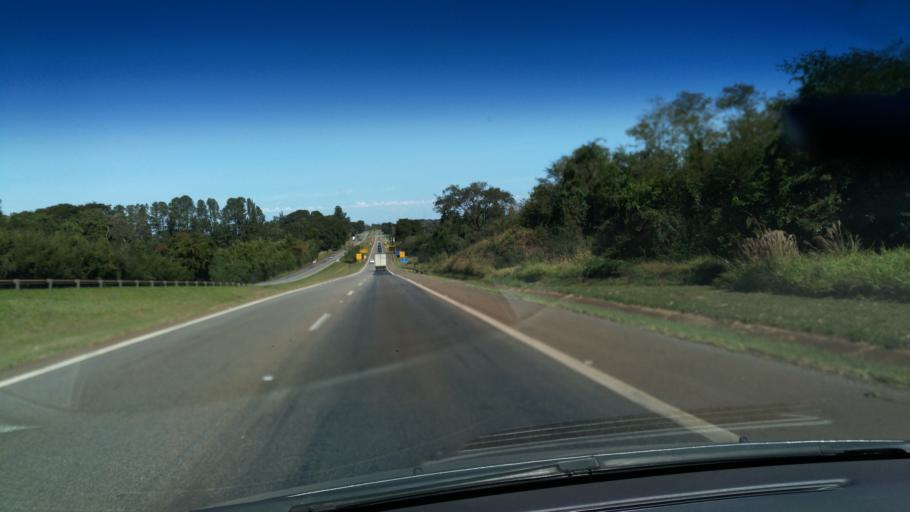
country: BR
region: Sao Paulo
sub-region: Santo Antonio De Posse
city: Santo Antonio de Posse
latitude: -22.5556
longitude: -46.9992
